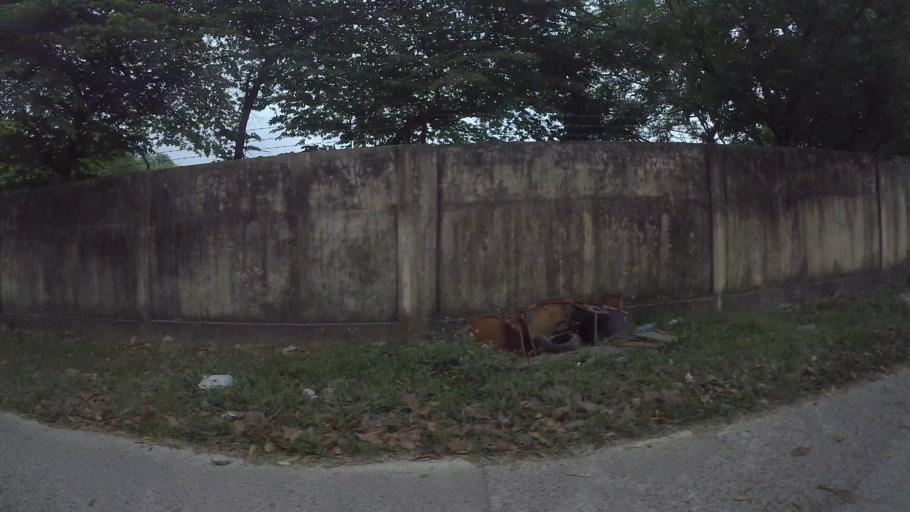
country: VN
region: Da Nang
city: Cam Le
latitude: 16.0331
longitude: 108.1771
